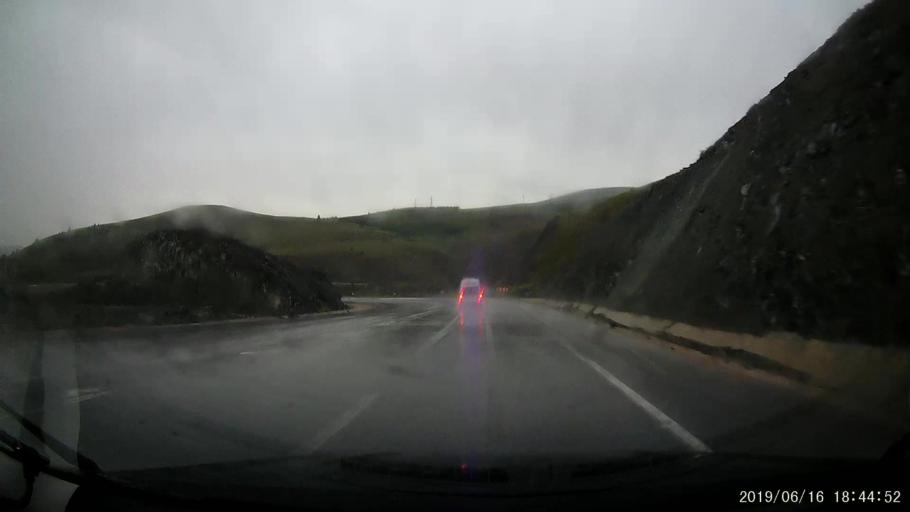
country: TR
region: Erzincan
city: Doganbeyli
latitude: 39.8708
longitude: 39.0660
